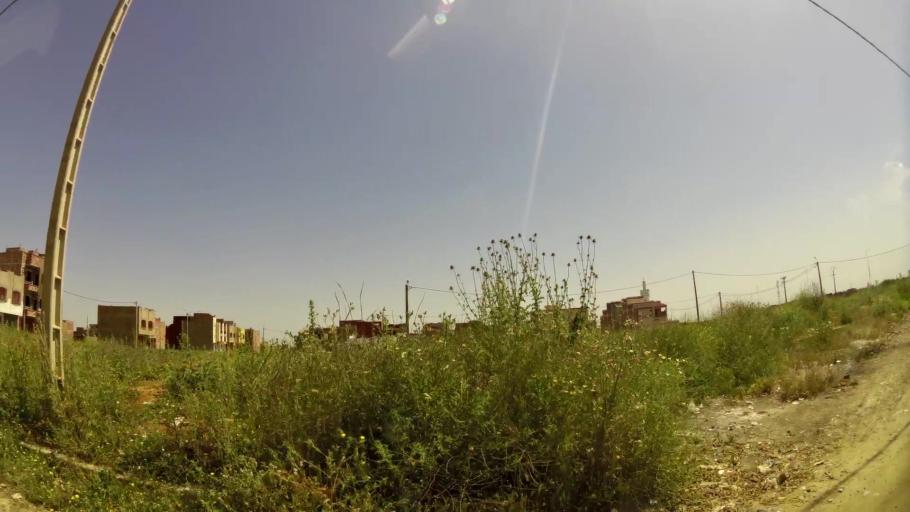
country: MA
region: Rabat-Sale-Zemmour-Zaer
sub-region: Khemisset
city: Khemisset
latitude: 33.8082
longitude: -6.0840
